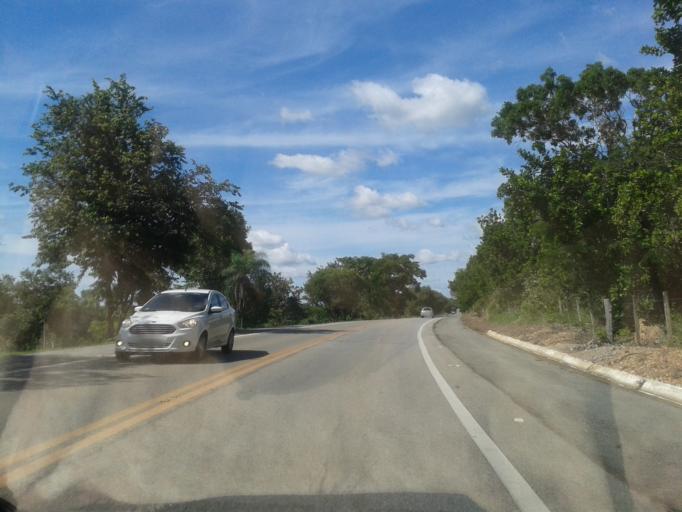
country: BR
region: Goias
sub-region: Itapuranga
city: Itapuranga
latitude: -15.3856
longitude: -50.3905
